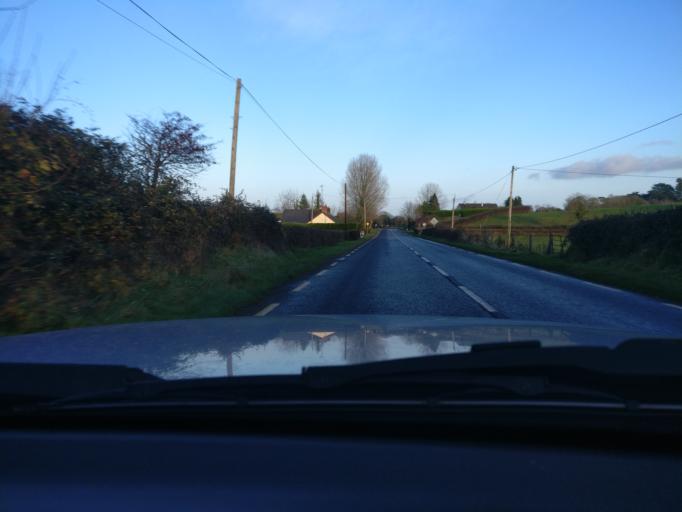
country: IE
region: Leinster
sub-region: Lu
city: Ardee
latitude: 53.8272
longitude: -6.6314
